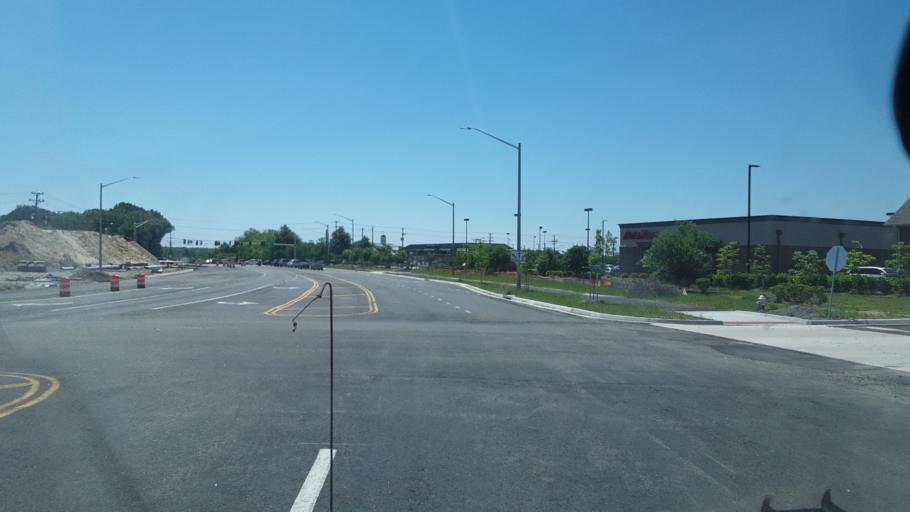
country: US
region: Virginia
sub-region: City of Virginia Beach
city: Virginia Beach
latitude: 36.7536
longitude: -76.0114
